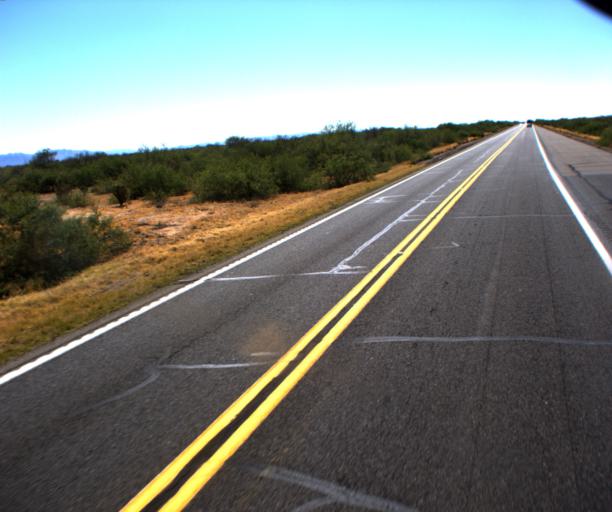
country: US
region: Arizona
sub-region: Yavapai County
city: Congress
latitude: 34.1424
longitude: -112.9779
